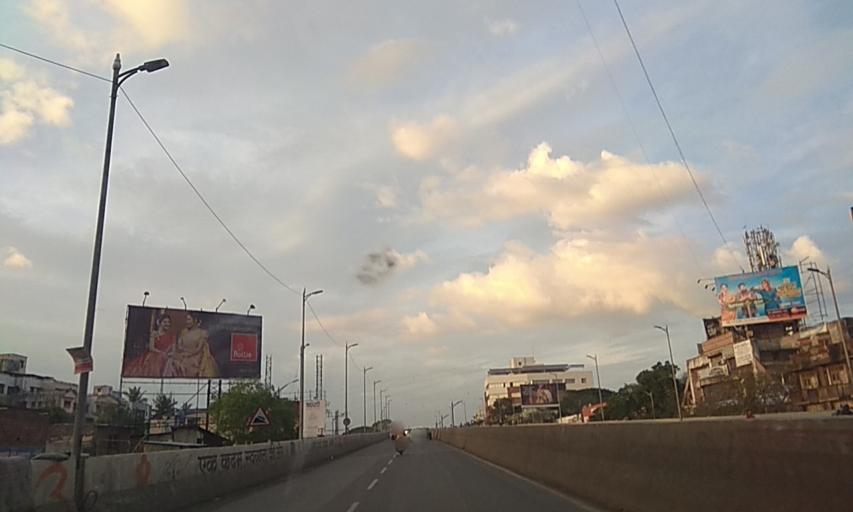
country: IN
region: Maharashtra
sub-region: Pune Division
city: Pune
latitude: 18.4946
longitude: 73.8577
